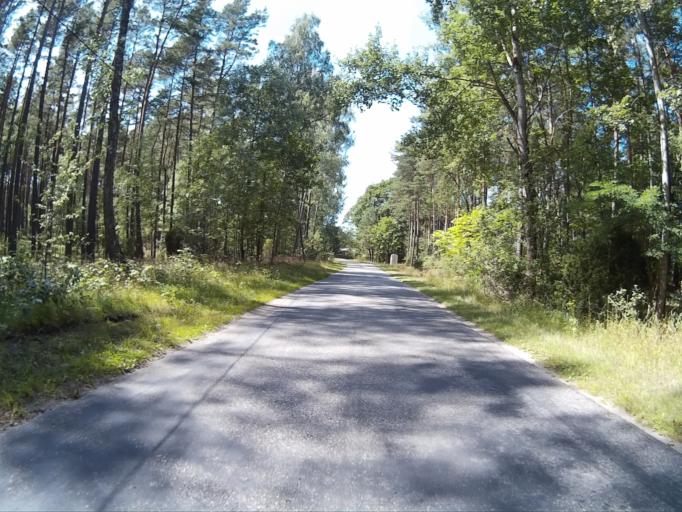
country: PL
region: Pomeranian Voivodeship
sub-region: Powiat chojnicki
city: Czersk
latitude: 53.7142
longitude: 17.9802
